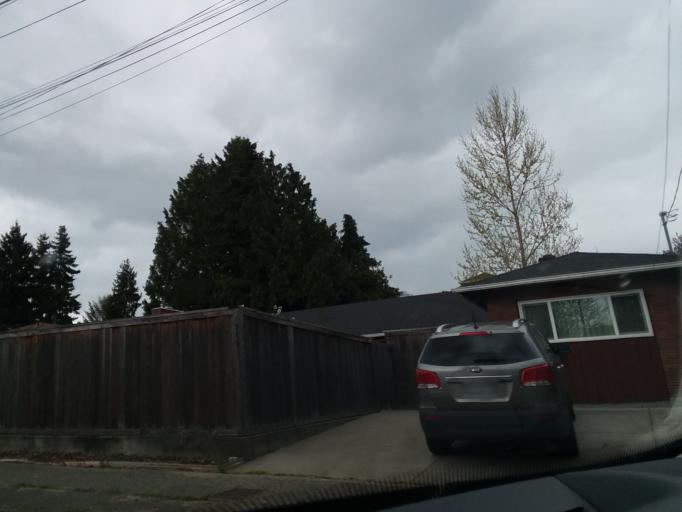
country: US
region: Washington
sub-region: King County
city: Seattle
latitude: 47.6770
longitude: -122.3006
